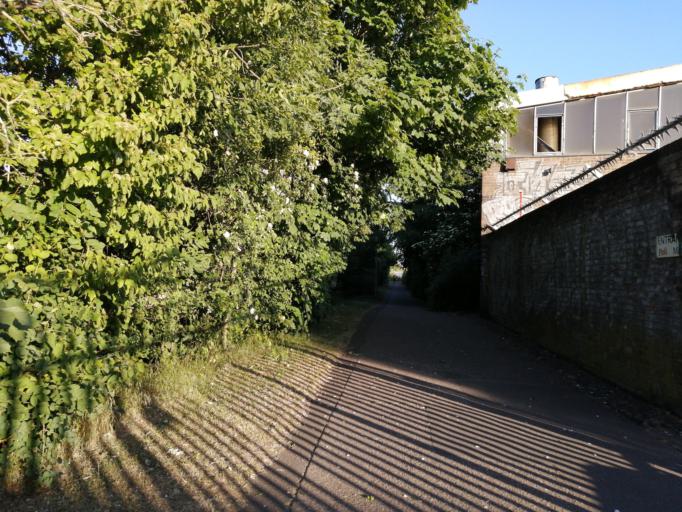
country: GB
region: England
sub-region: Peterborough
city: Peterborough
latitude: 52.5965
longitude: -0.2655
